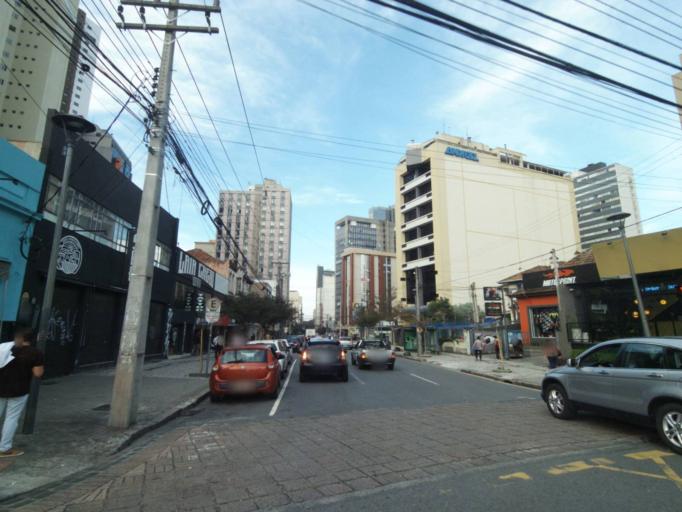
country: BR
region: Parana
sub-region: Curitiba
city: Curitiba
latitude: -25.4355
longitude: -49.2827
